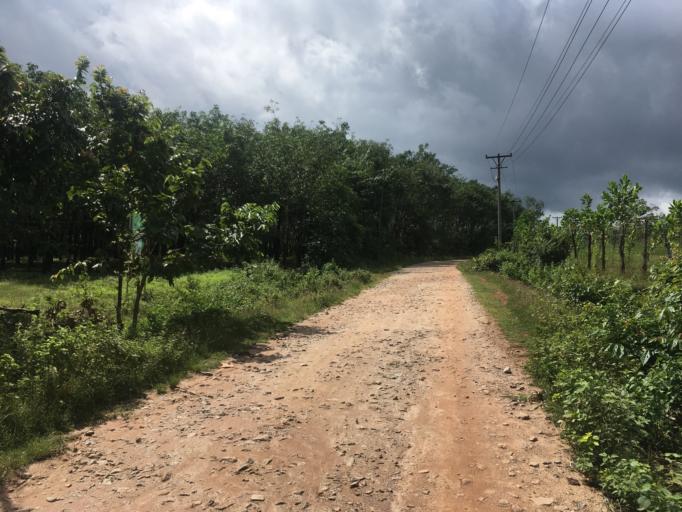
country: MM
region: Mon
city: Mawlamyine
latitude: 16.4634
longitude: 97.6905
